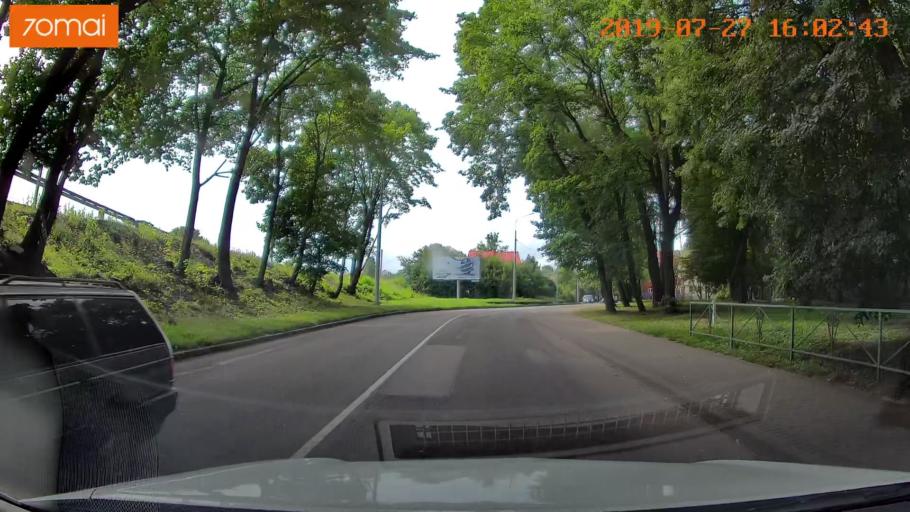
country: RU
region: Kaliningrad
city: Chernyakhovsk
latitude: 54.6304
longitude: 21.8075
